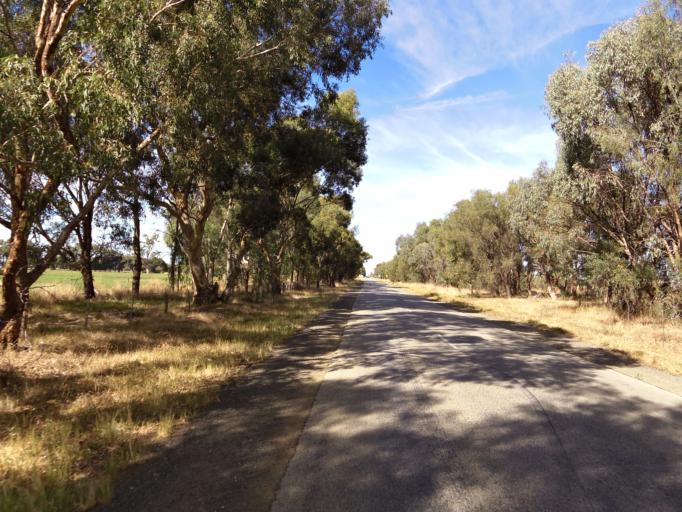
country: AU
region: Victoria
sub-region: Campaspe
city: Echuca
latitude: -36.2582
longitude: 144.5358
